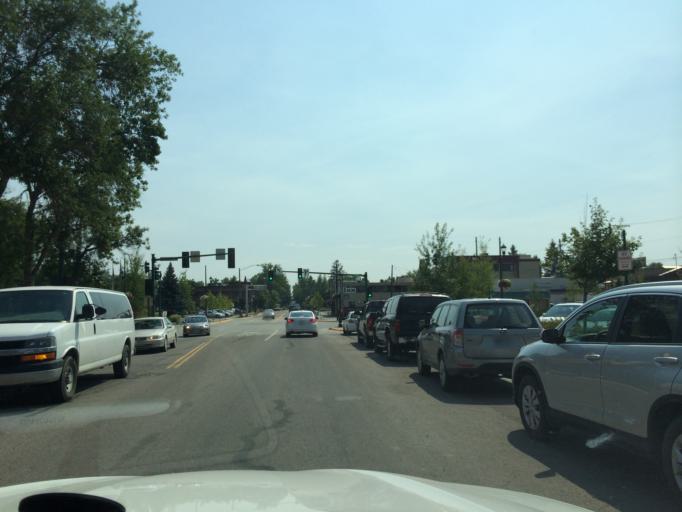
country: US
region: Montana
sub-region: Flathead County
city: Whitefish
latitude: 48.4111
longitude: -114.3353
